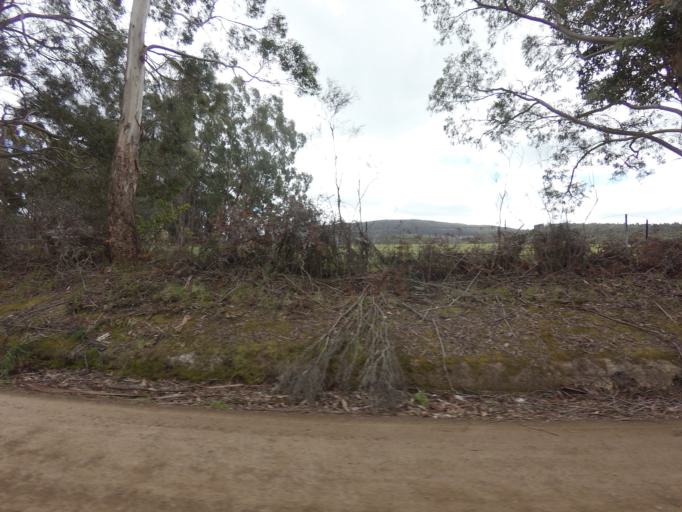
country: AU
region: Tasmania
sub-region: Huon Valley
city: Geeveston
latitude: -43.4265
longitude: 146.9967
